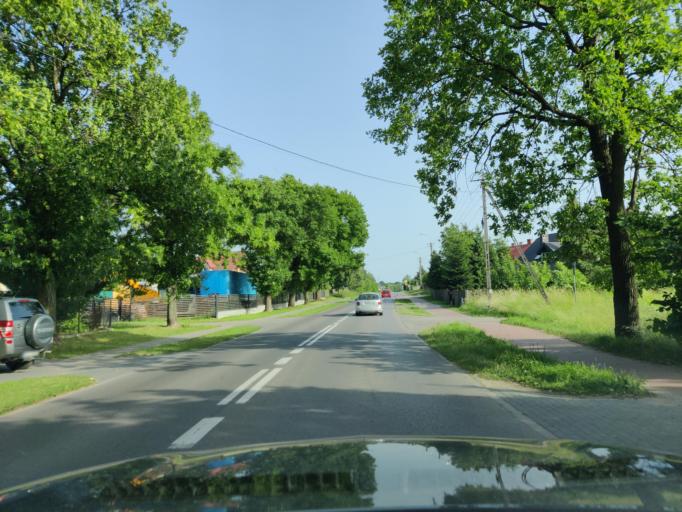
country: PL
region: Masovian Voivodeship
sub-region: Powiat wyszkowski
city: Wyszkow
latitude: 52.6485
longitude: 21.4498
